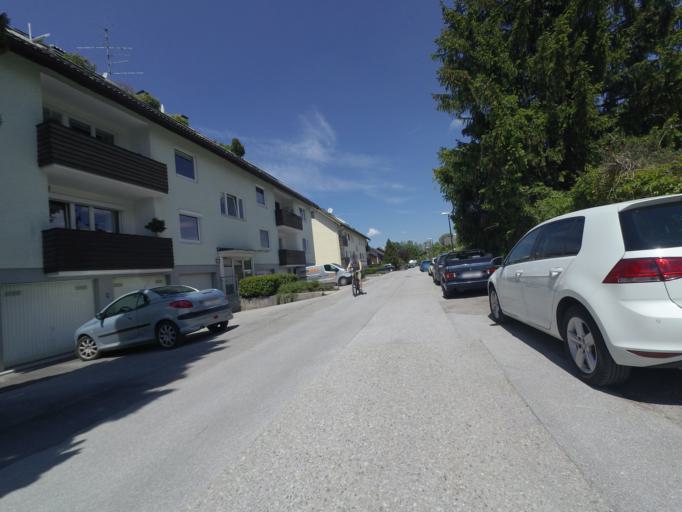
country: AT
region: Salzburg
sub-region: Salzburg Stadt
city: Salzburg
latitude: 47.7748
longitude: 13.0353
